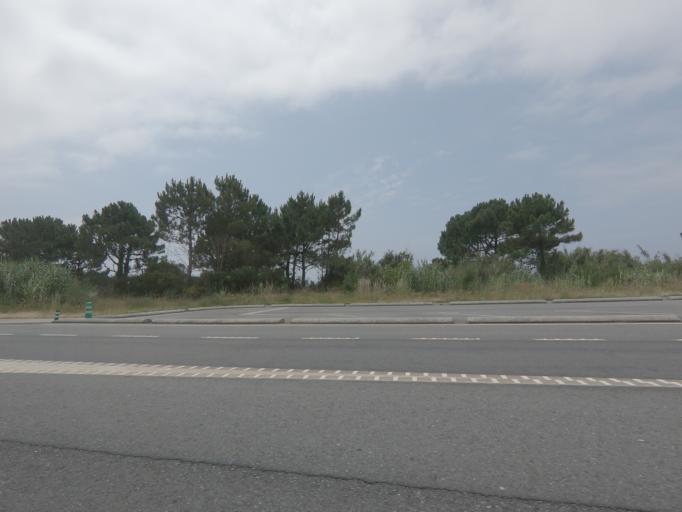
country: ES
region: Galicia
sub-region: Provincia de Pontevedra
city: Oia
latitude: 41.9715
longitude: -8.8841
